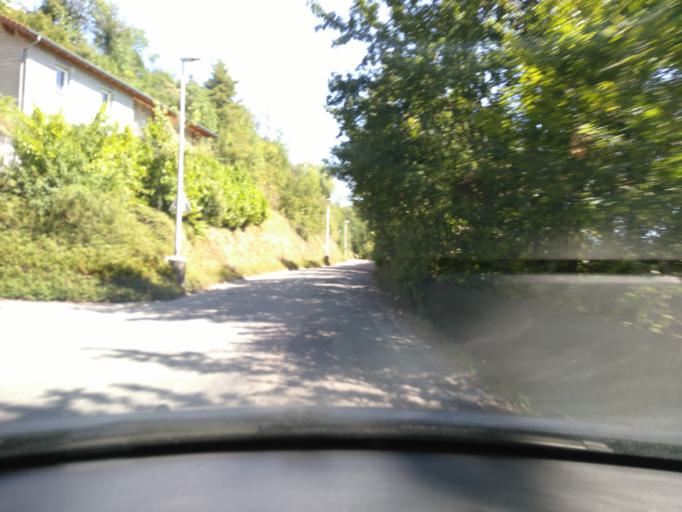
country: FR
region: Rhone-Alpes
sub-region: Departement de l'Isere
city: Meylan
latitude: 45.2266
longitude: 5.7821
